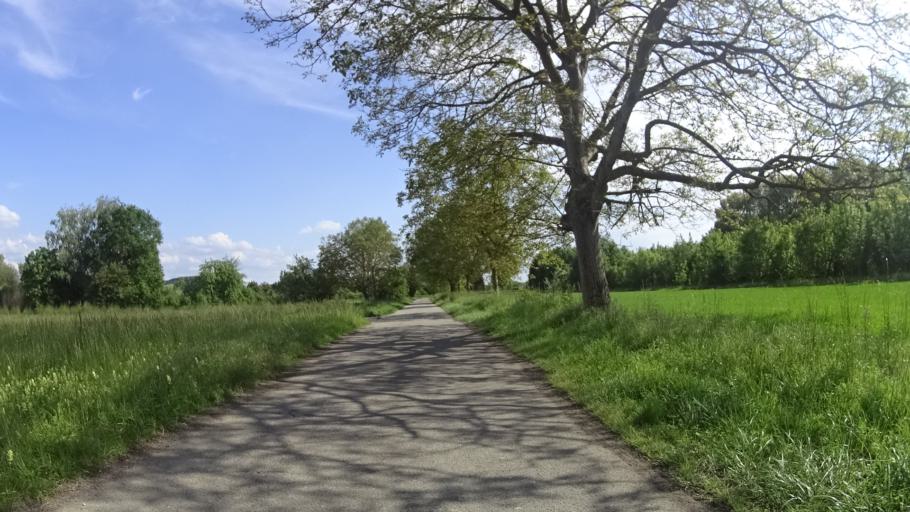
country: DE
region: Baden-Wuerttemberg
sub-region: Freiburg Region
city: Vogtsburg
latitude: 48.0915
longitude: 7.5939
